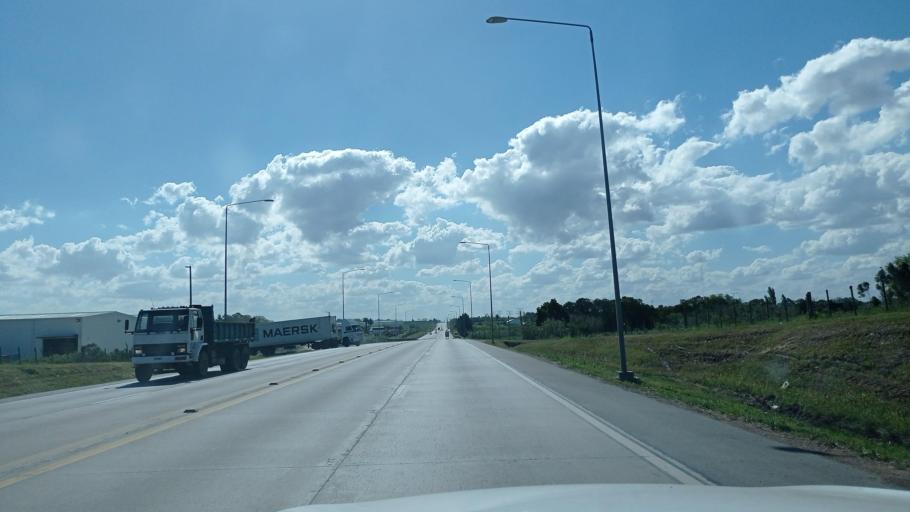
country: UY
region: Canelones
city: La Paz
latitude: -34.7951
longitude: -56.2021
